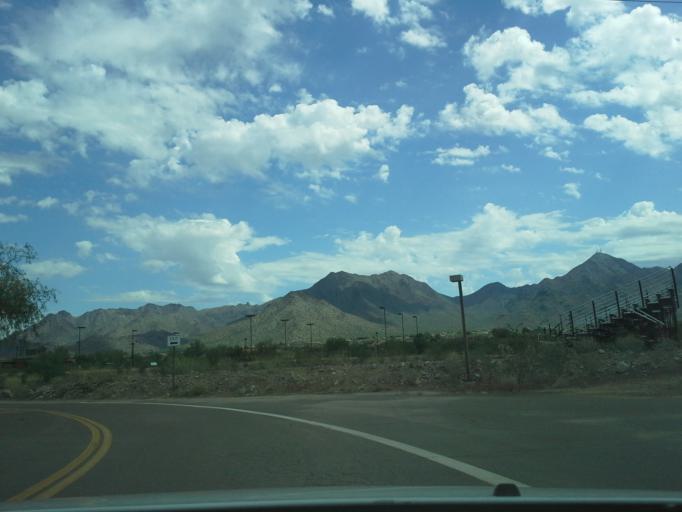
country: US
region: Arizona
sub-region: Maricopa County
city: Paradise Valley
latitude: 33.6291
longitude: -111.8711
